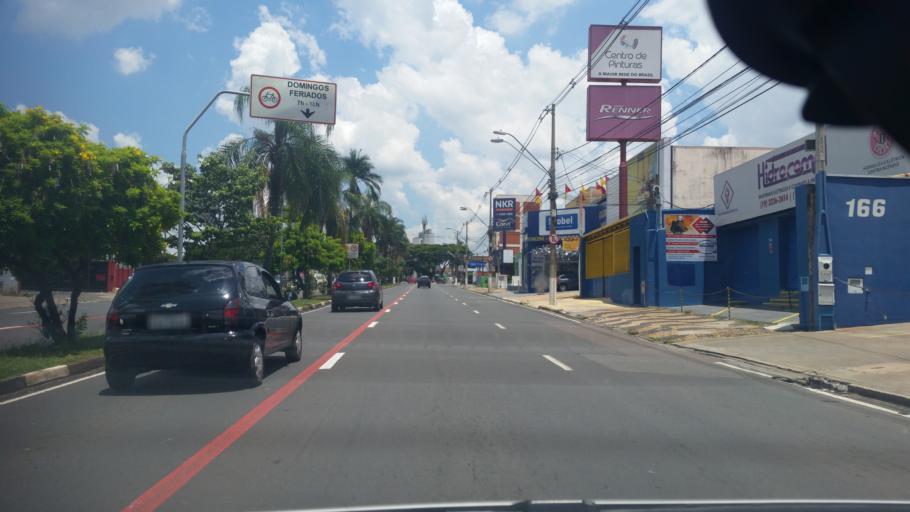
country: BR
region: Sao Paulo
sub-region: Campinas
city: Campinas
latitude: -22.8762
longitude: -47.0457
